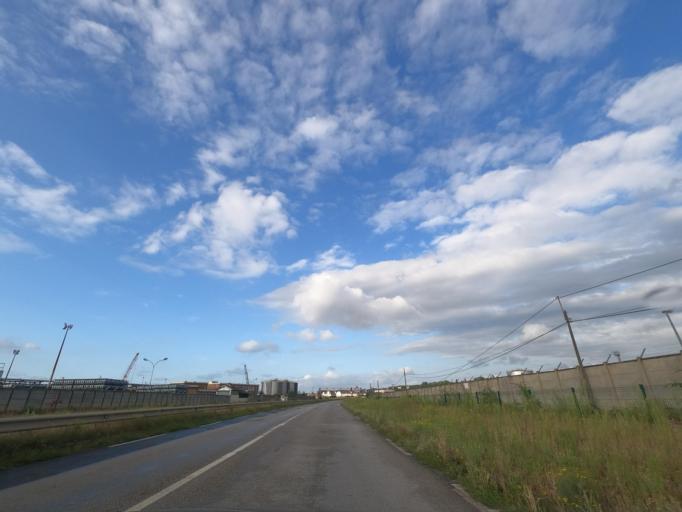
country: FR
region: Haute-Normandie
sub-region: Departement de la Seine-Maritime
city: Petit-Couronne
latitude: 49.3776
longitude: 1.0111
